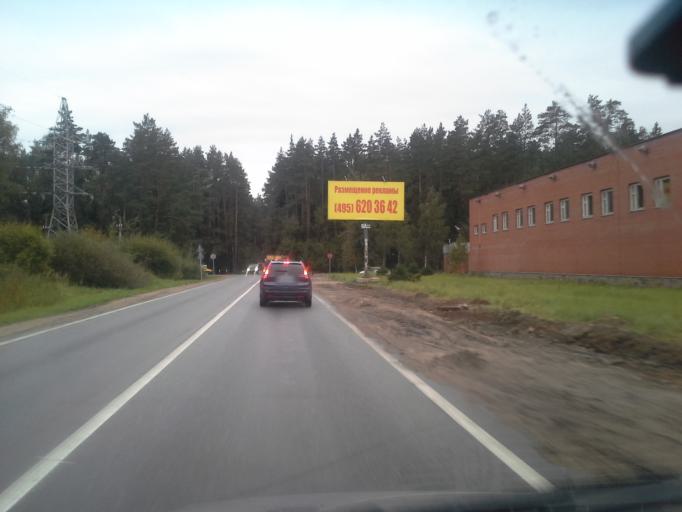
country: RU
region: Moskovskaya
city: Petrovo-Dal'neye
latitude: 55.7749
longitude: 37.1633
